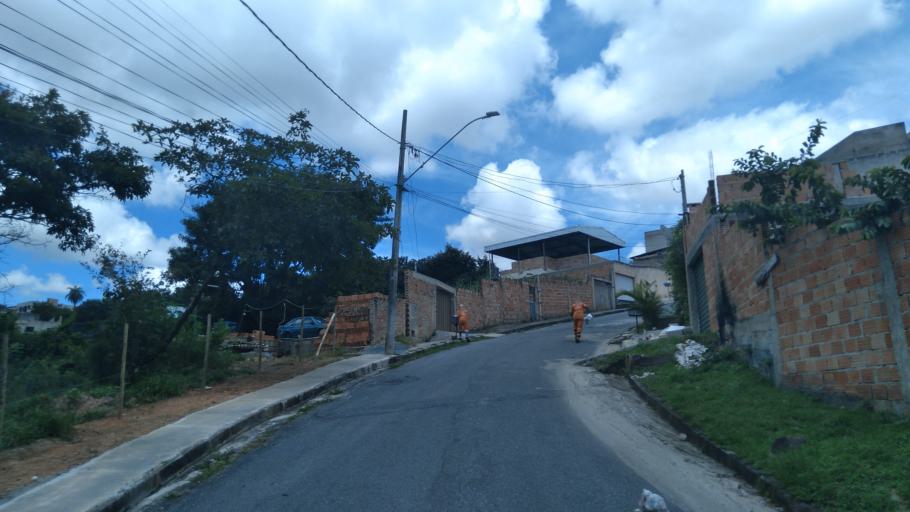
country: BR
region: Minas Gerais
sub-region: Belo Horizonte
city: Belo Horizonte
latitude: -19.8554
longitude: -43.8803
